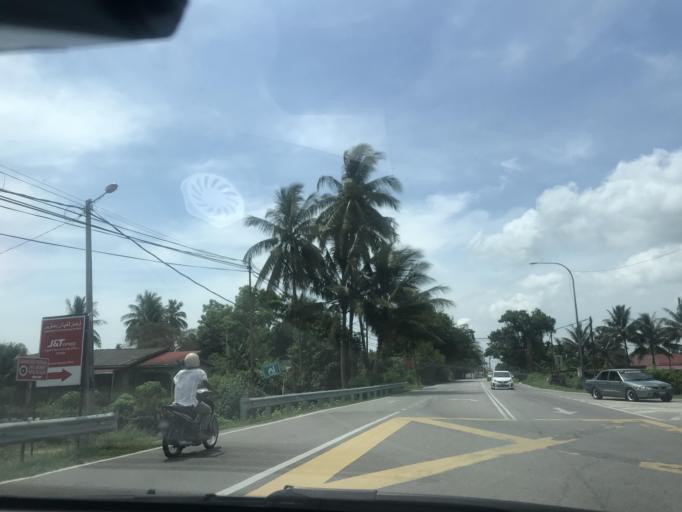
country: MY
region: Kelantan
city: Tumpat
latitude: 6.2021
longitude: 102.1564
